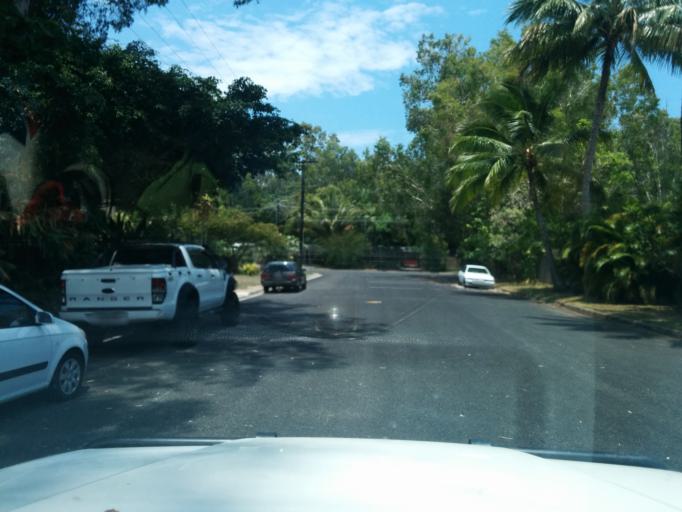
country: AU
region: Queensland
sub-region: Cairns
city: Yorkeys Knob
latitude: -16.8393
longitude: 145.7366
